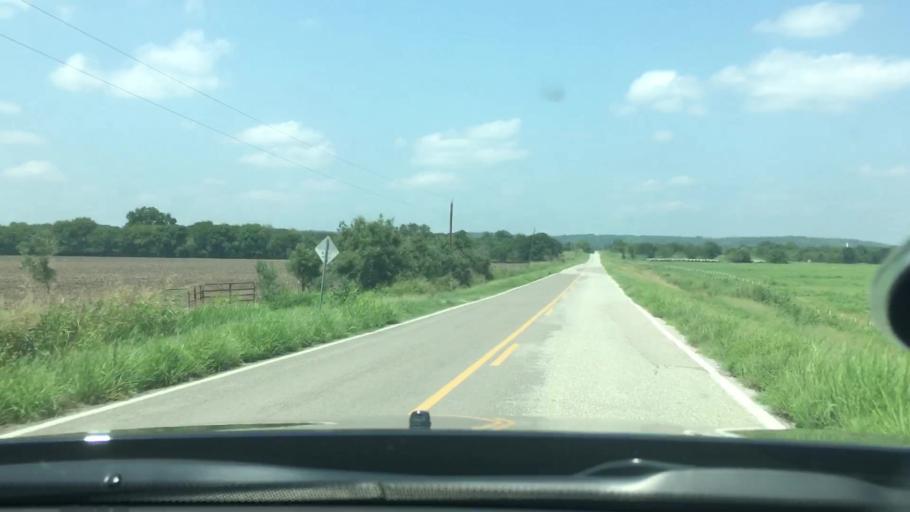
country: US
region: Oklahoma
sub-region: Johnston County
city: Tishomingo
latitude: 34.3909
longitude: -96.4962
